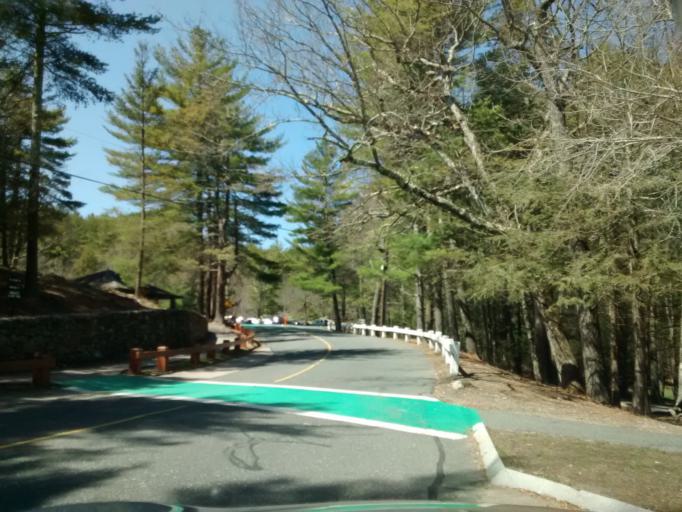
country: US
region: Massachusetts
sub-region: Worcester County
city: Whitinsville
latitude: 42.1291
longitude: -71.7140
